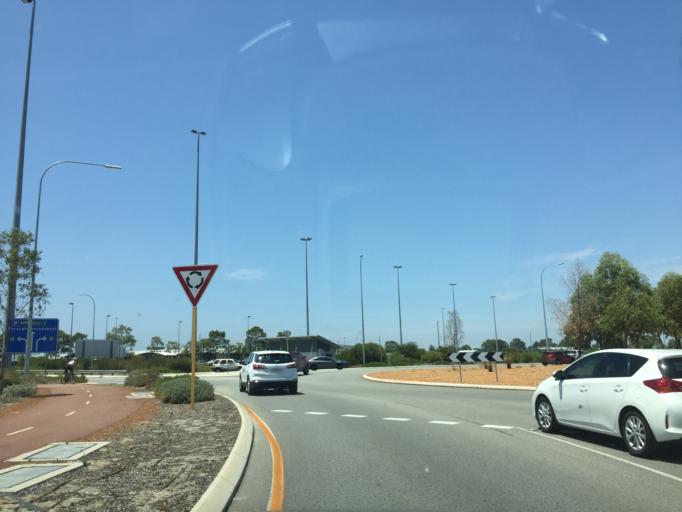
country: AU
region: Western Australia
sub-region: Belmont
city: Redcliffe
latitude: -31.9551
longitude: 115.9693
